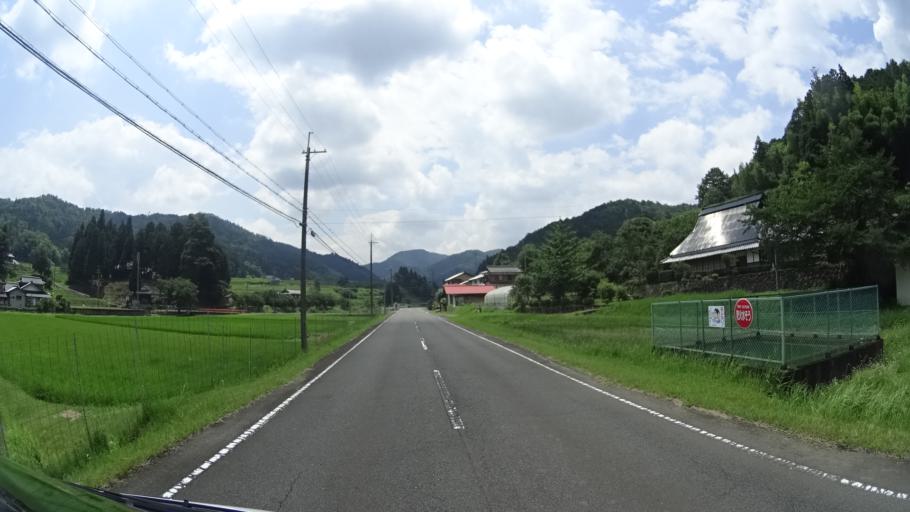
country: JP
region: Kyoto
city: Ayabe
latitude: 35.2010
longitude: 135.2224
